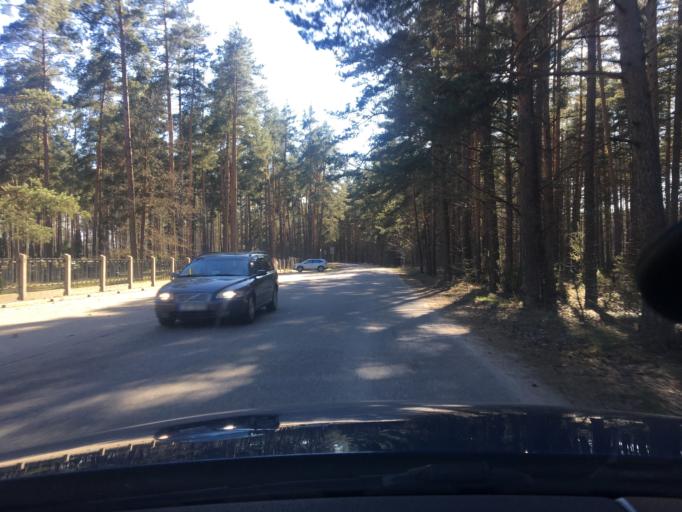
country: LV
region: Salaspils
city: Salaspils
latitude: 56.8639
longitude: 24.3084
